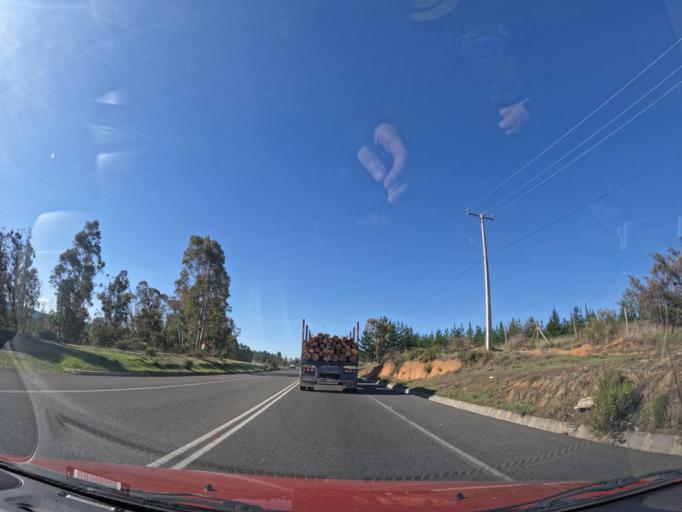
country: CL
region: Maule
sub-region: Provincia de Cauquenes
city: Cauquenes
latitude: -35.9316
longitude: -72.1913
